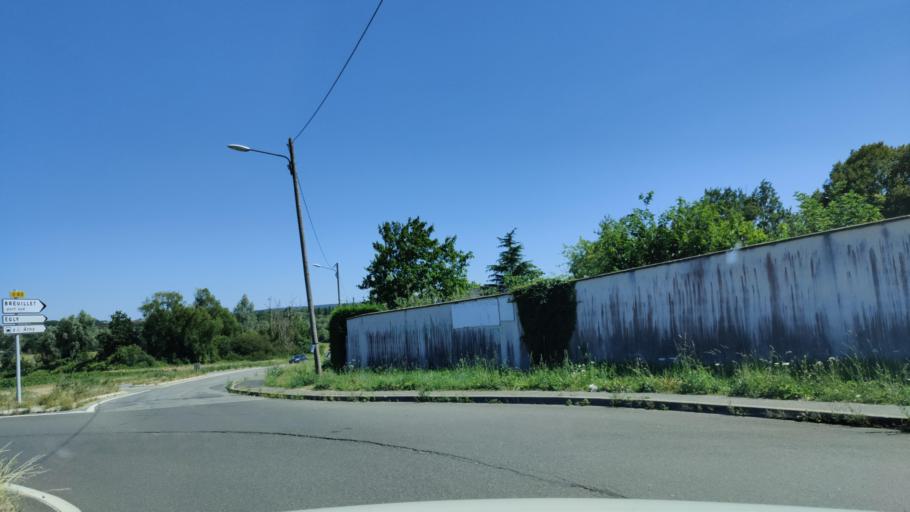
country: FR
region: Ile-de-France
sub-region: Departement de l'Essonne
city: Bruyeres-le-Chatel
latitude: 48.5863
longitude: 2.1909
